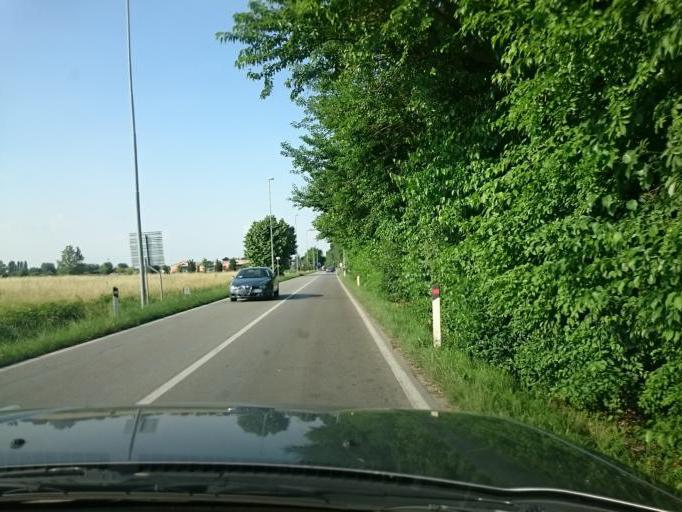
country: IT
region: Veneto
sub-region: Provincia di Padova
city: Abano Terme
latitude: 45.3446
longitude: 11.8006
